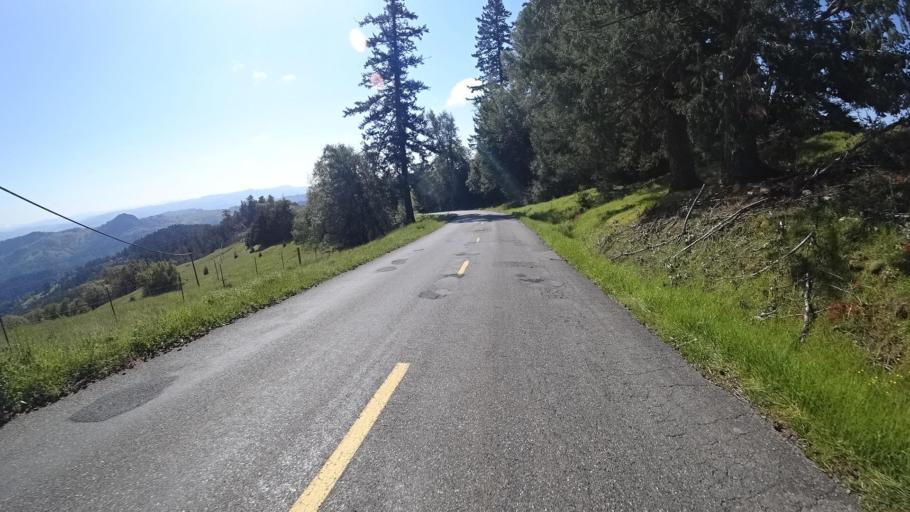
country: US
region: California
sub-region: Humboldt County
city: Redway
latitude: 40.0866
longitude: -123.6725
